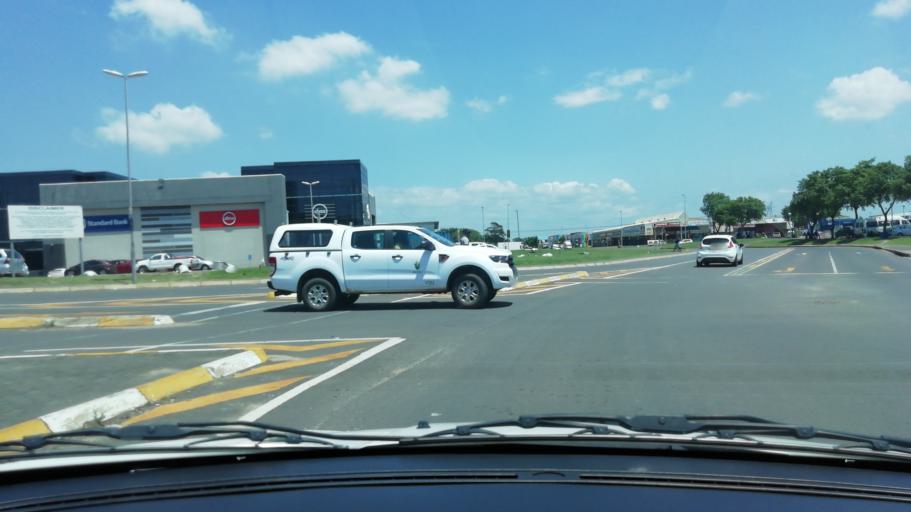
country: ZA
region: KwaZulu-Natal
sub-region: uThungulu District Municipality
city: Richards Bay
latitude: -28.7541
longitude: 32.0484
